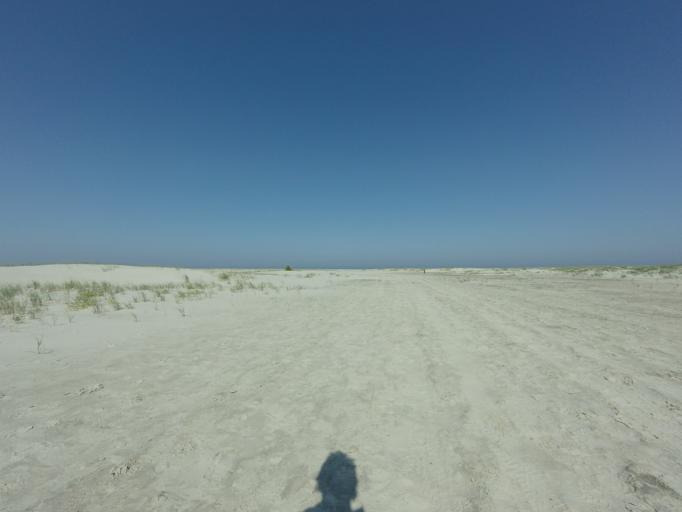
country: NL
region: Friesland
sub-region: Gemeente Schiermonnikoog
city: Schiermonnikoog
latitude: 53.5025
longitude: 6.2457
